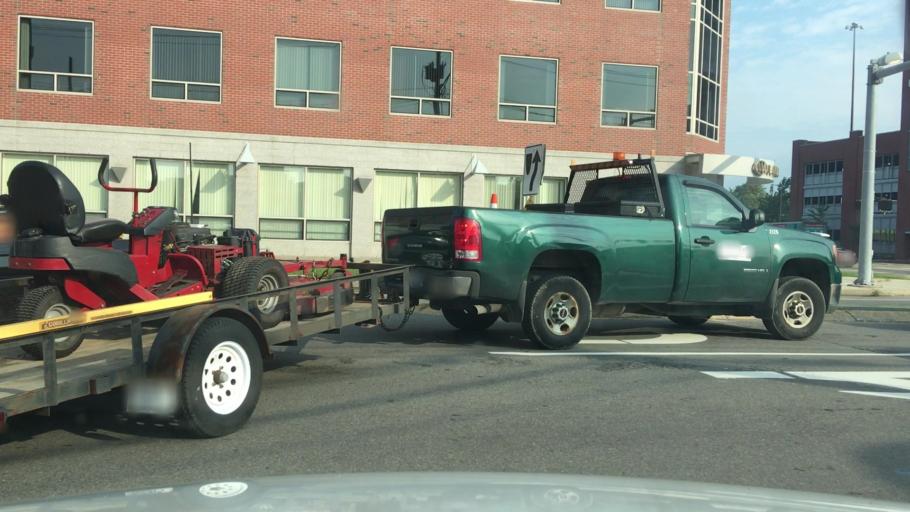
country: US
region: Maine
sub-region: Cumberland County
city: Portland
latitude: 43.6616
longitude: -70.2656
